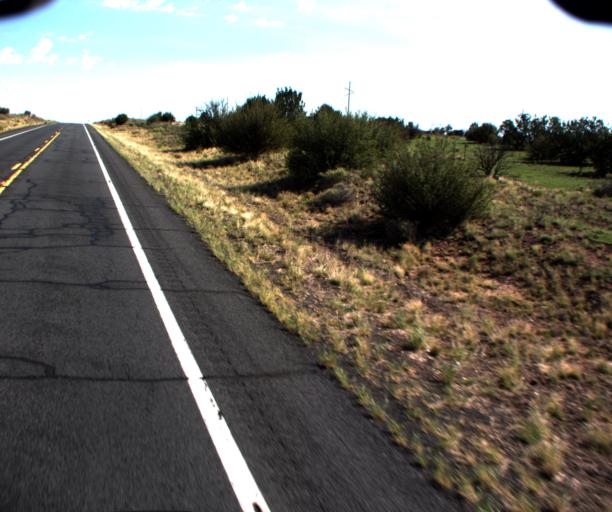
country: US
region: Arizona
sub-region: Coconino County
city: Williams
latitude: 35.5238
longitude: -112.1684
